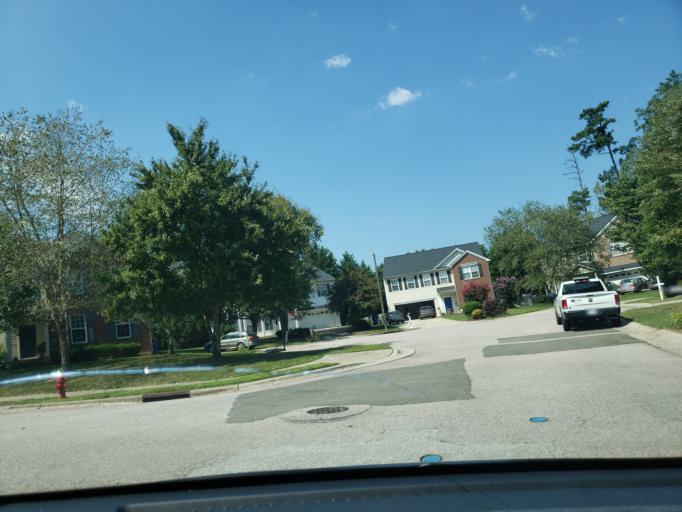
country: US
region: North Carolina
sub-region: Durham County
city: Durham
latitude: 35.9066
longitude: -78.9282
